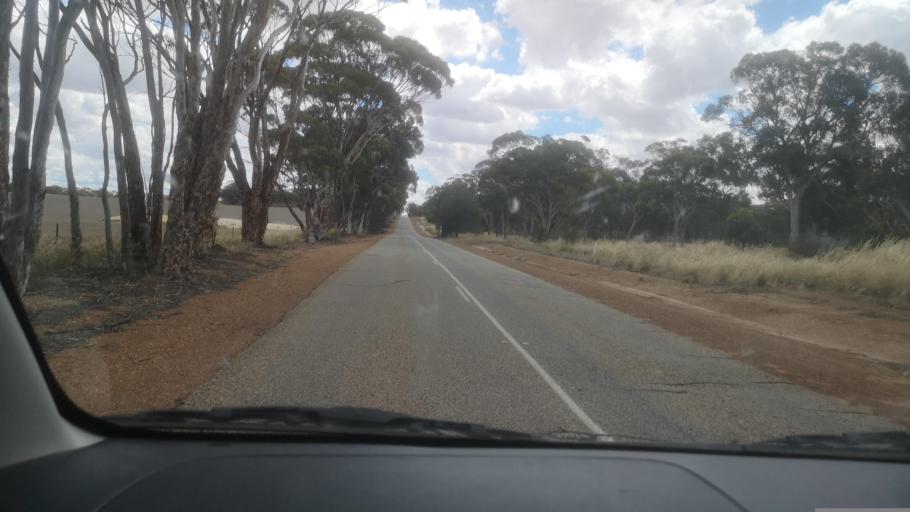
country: AU
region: Western Australia
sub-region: Beverley
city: Beverley
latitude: -31.9899
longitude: 117.1148
